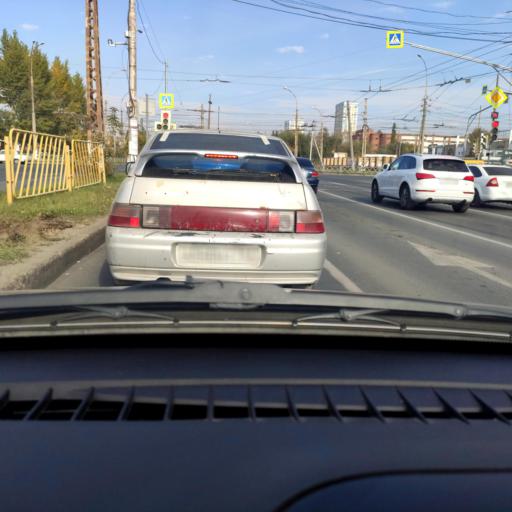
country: RU
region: Samara
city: Tol'yatti
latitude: 53.5358
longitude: 49.2990
